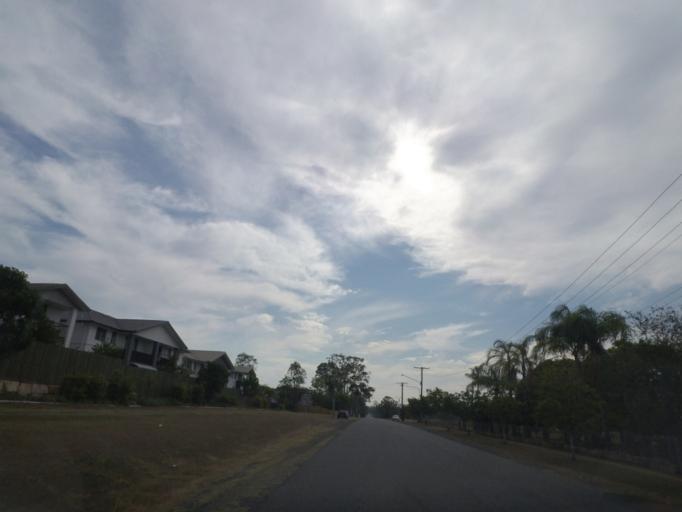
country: AU
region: Queensland
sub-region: Brisbane
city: Richlands
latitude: -27.5924
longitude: 152.9569
